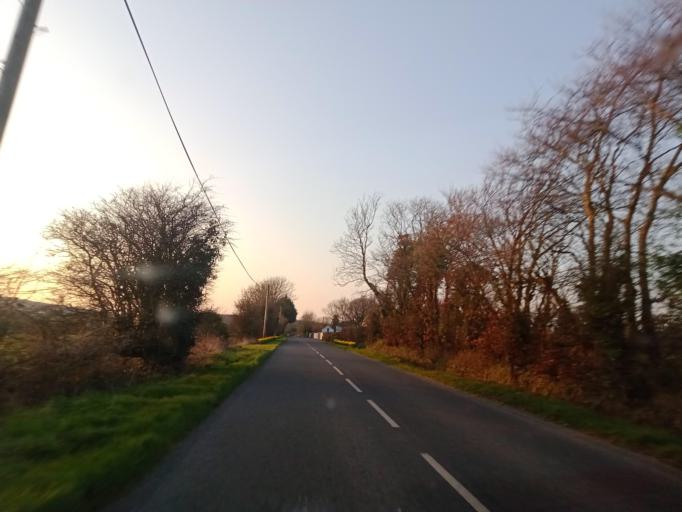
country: IE
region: Leinster
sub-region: Kilkenny
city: Castlecomer
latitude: 52.8353
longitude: -7.2393
